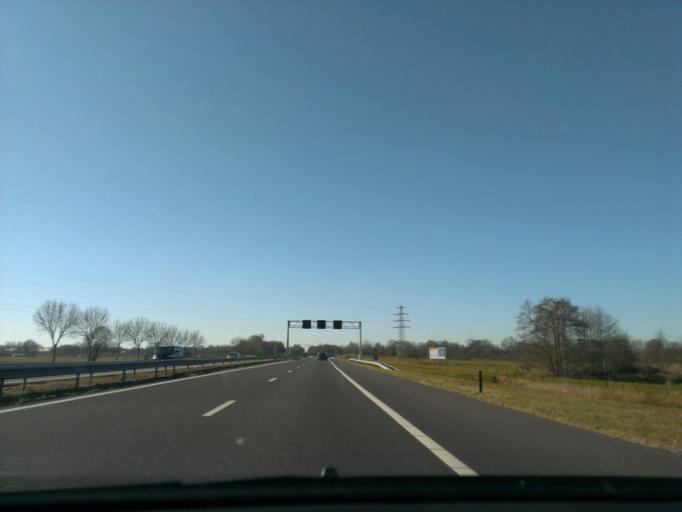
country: NL
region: Drenthe
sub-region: Gemeente Meppel
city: Meppel
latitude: 52.6846
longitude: 6.2013
